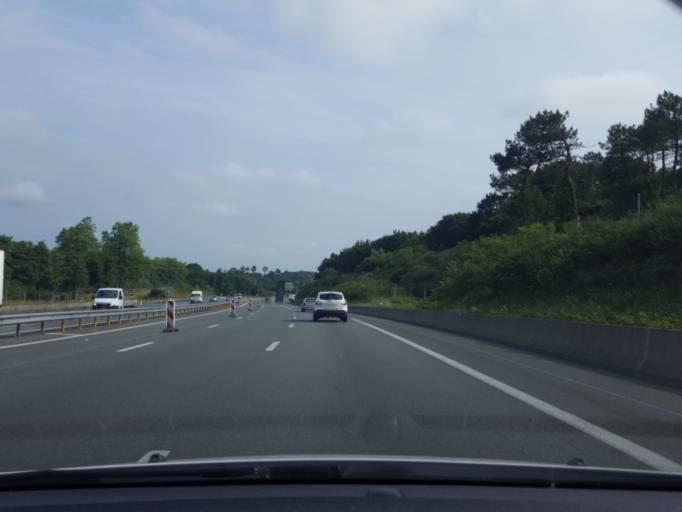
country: FR
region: Aquitaine
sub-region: Departement des Landes
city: Tarnos
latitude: 43.5350
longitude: -1.4311
